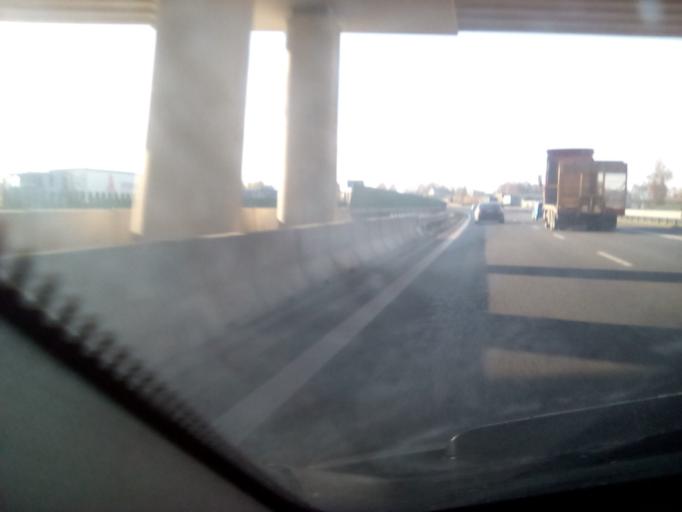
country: PL
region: Masovian Voivodeship
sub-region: Powiat grojecki
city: Grojec
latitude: 51.8701
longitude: 20.8518
